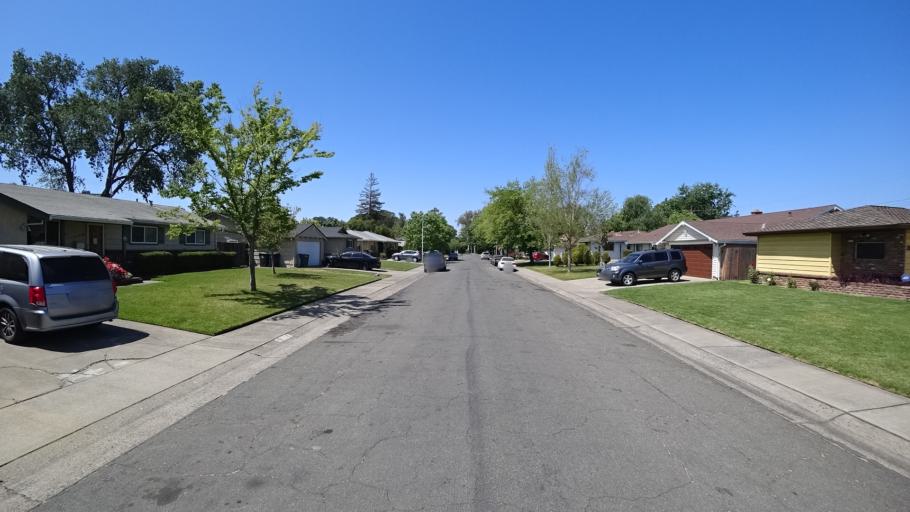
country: US
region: California
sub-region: Sacramento County
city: Parkway
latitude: 38.4997
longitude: -121.4898
